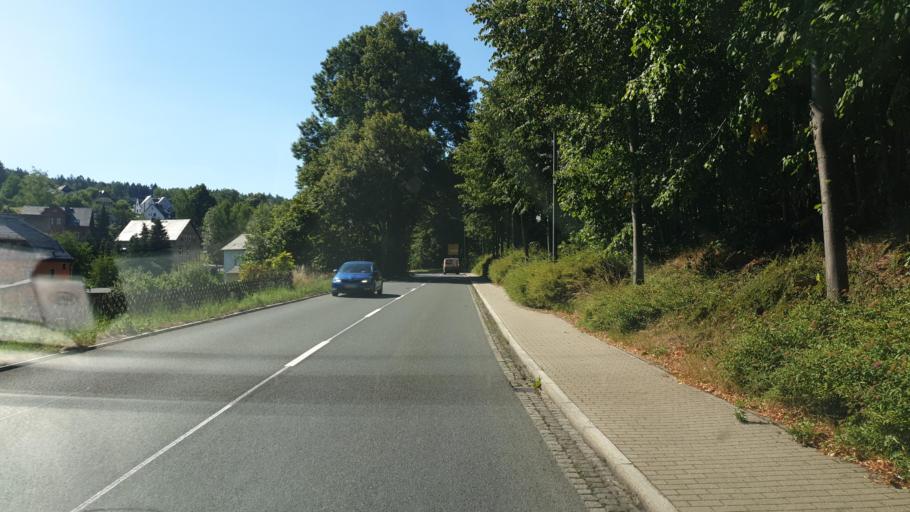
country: DE
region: Saxony
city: Auerbach
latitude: 50.5018
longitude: 12.4346
